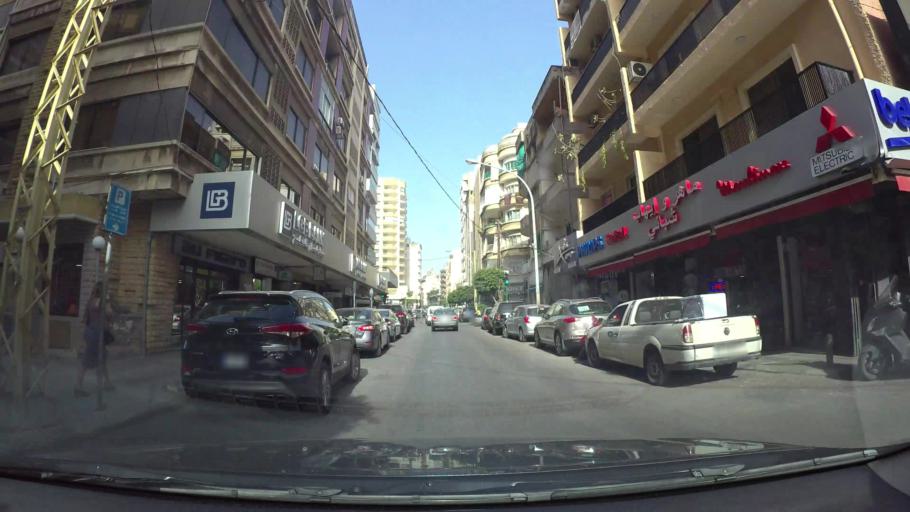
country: LB
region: Beyrouth
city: Ra's Bayrut
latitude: 33.8940
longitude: 35.4803
